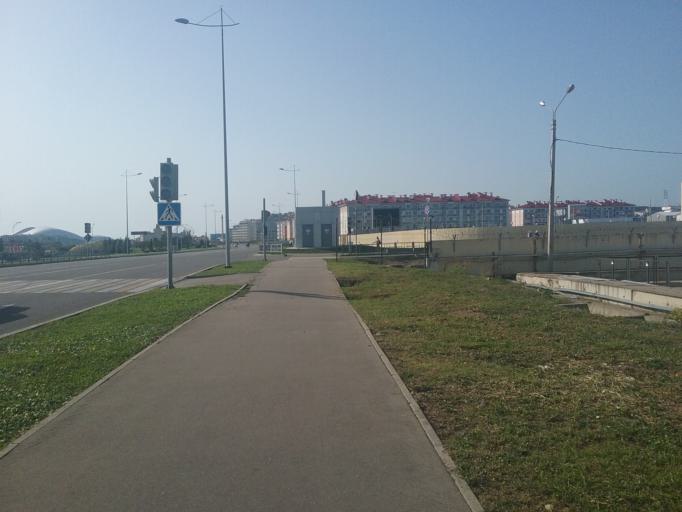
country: RU
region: Krasnodarskiy
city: Vysokoye
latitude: 43.3982
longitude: 39.9839
